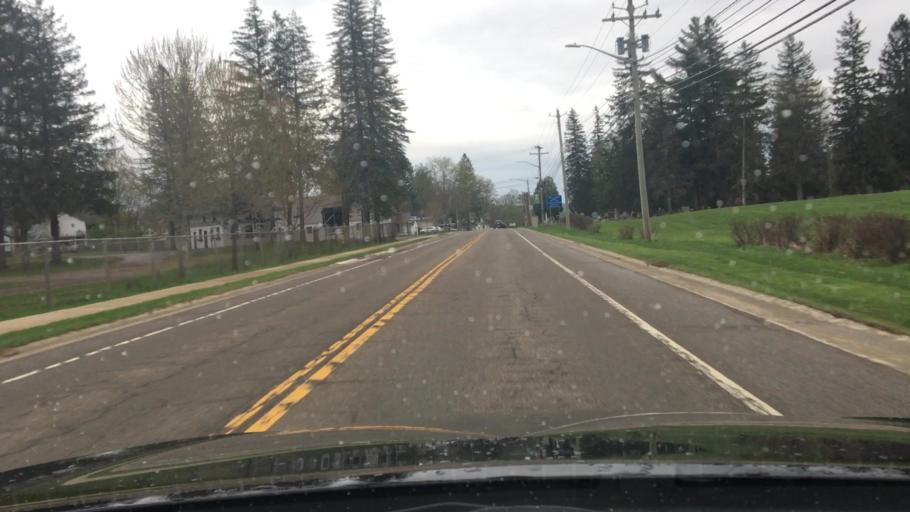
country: US
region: New York
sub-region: Cattaraugus County
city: Little Valley
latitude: 42.2531
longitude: -78.8068
